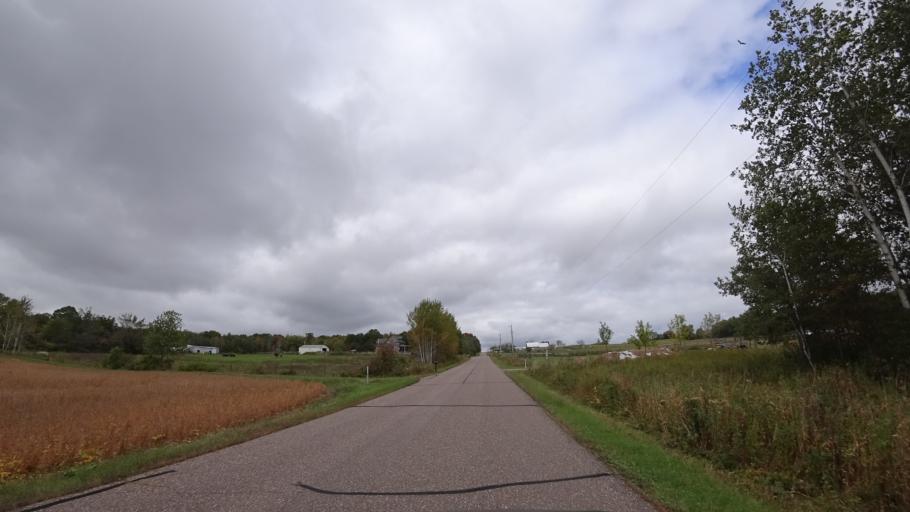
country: US
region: Wisconsin
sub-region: Chippewa County
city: Lake Wissota
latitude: 44.9874
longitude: -91.2869
